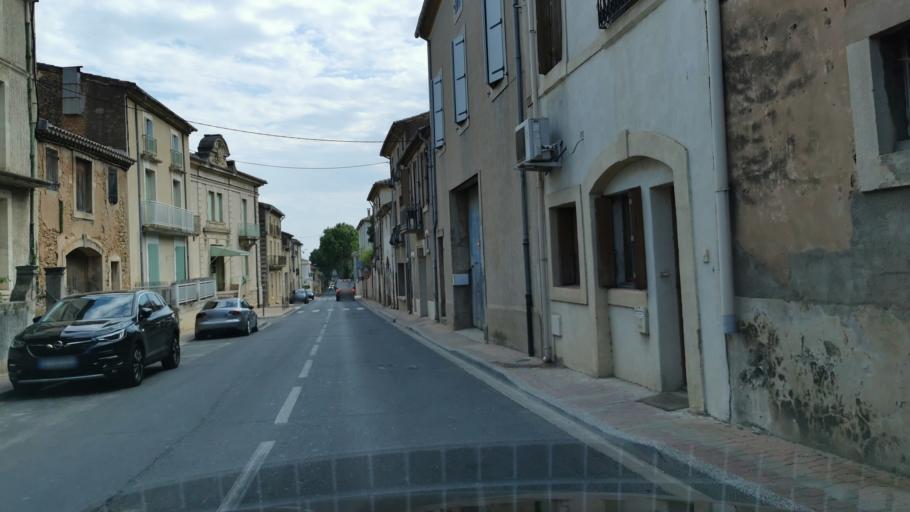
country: FR
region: Languedoc-Roussillon
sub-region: Departement de l'Herault
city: Puisserguier
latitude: 43.3665
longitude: 3.0402
